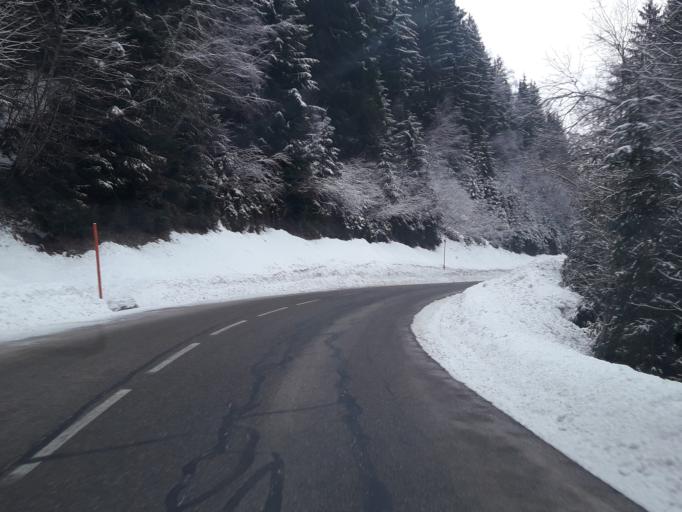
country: FR
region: Rhone-Alpes
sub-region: Departement de l'Isere
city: Theys
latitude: 45.2712
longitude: 6.0086
